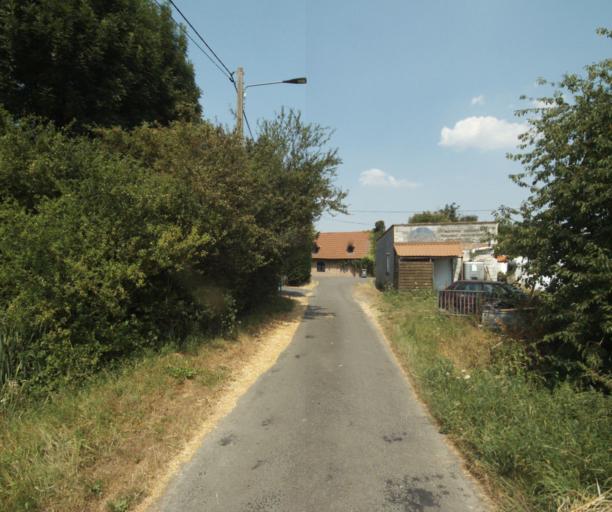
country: FR
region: Nord-Pas-de-Calais
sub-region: Departement du Nord
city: Quesnoy-sur-Deule
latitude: 50.7101
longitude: 3.0285
